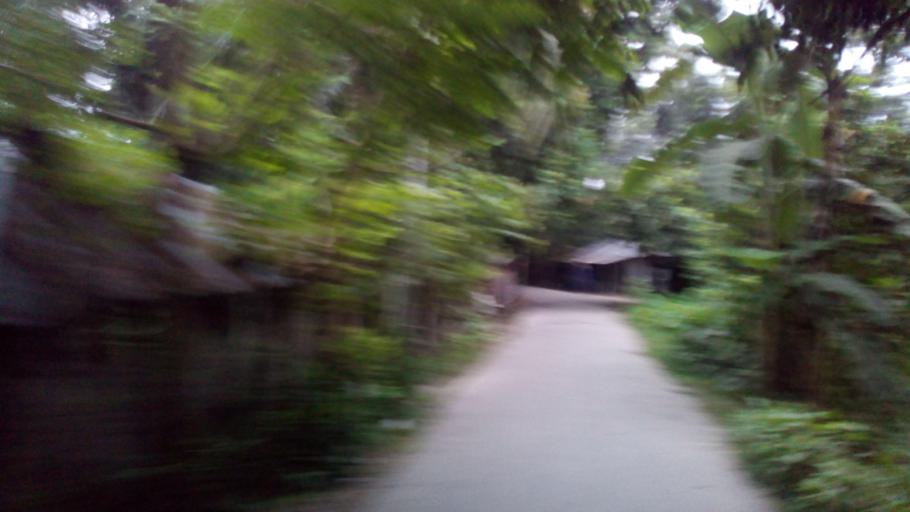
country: BD
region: Khulna
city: Phultala
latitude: 22.7582
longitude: 89.4082
